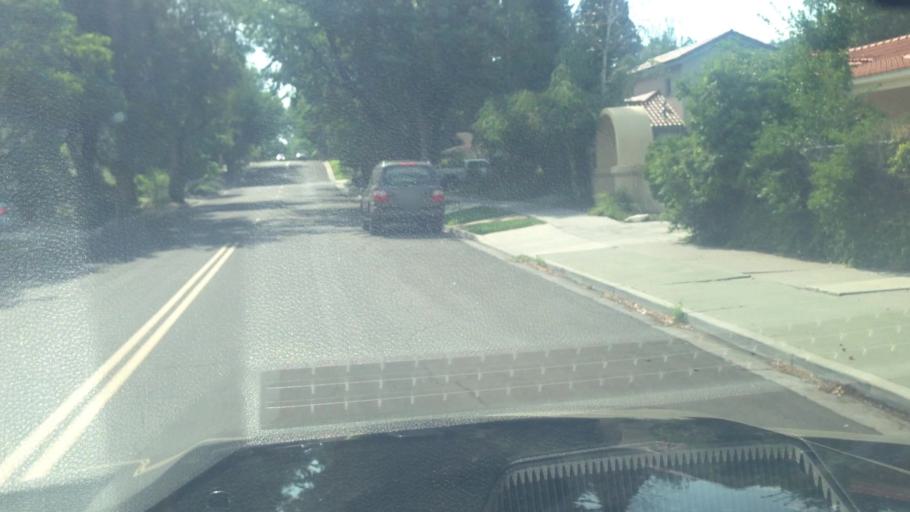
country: US
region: Nevada
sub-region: Washoe County
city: Reno
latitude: 39.5148
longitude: -119.8202
